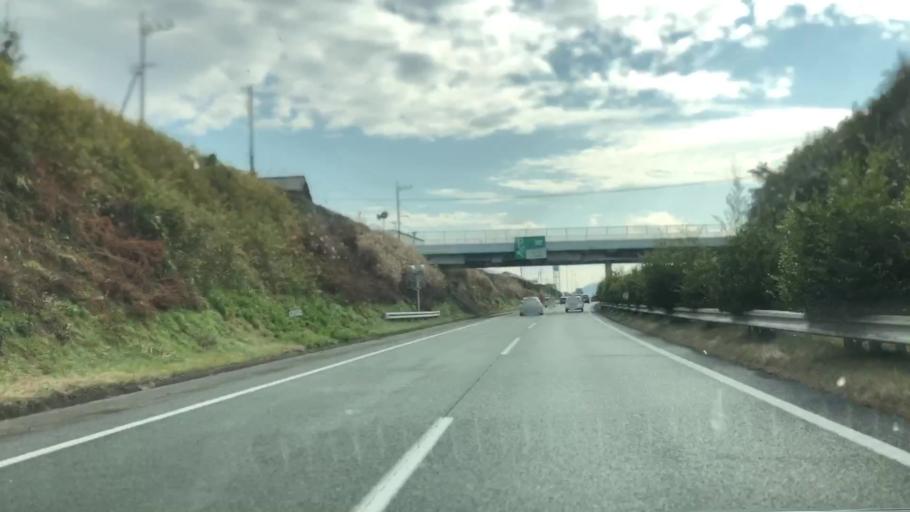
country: JP
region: Fukuoka
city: Setakamachi-takayanagi
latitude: 33.1328
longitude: 130.5170
